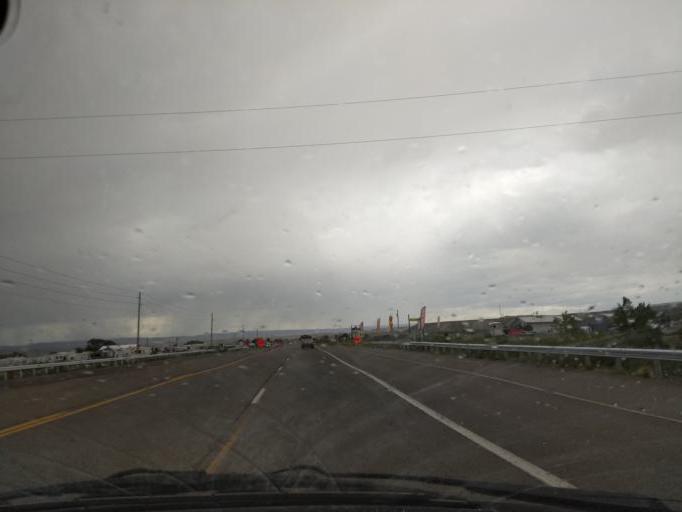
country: US
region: Colorado
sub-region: Delta County
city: Delta
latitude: 38.7628
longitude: -108.0996
